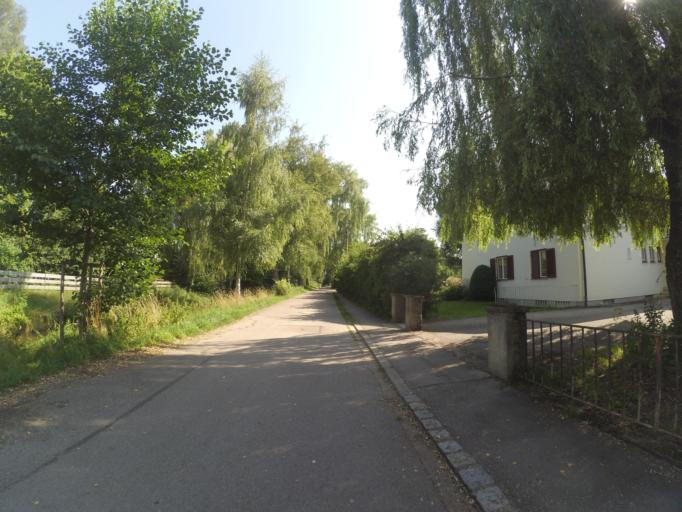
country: DE
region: Bavaria
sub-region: Swabia
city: Buchloe
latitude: 48.0328
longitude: 10.7253
